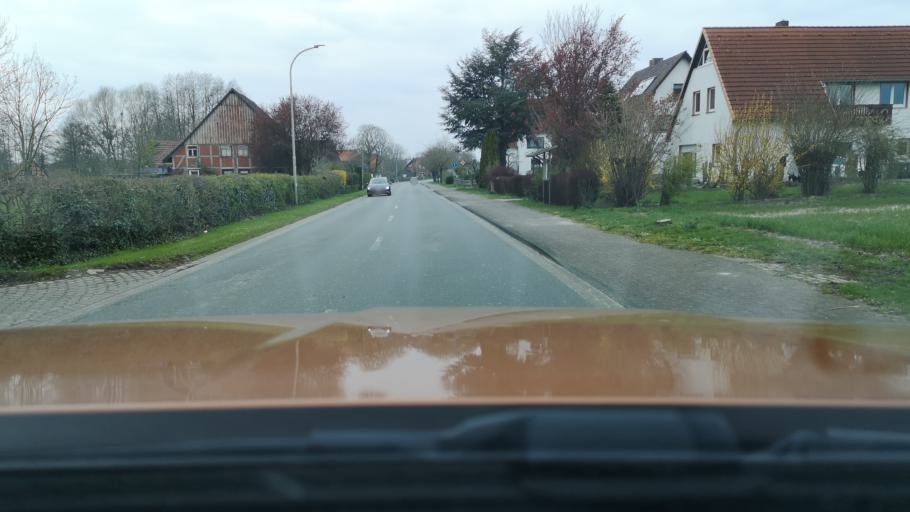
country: DE
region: Lower Saxony
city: Obernkirchen
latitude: 52.2846
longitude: 9.1170
